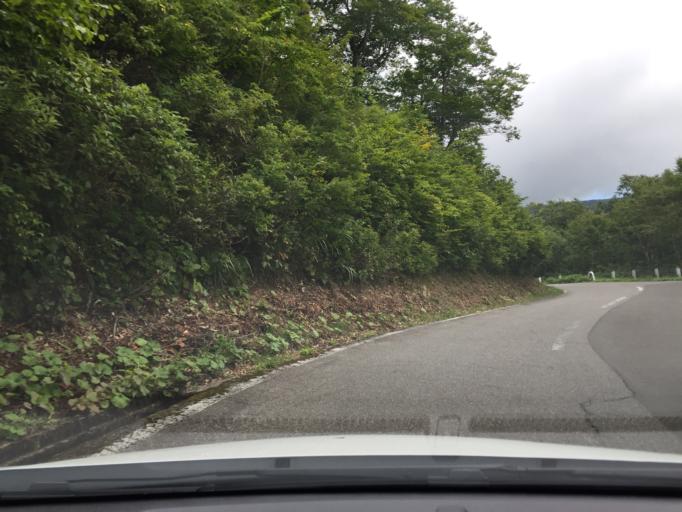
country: JP
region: Fukushima
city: Inawashiro
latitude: 37.6794
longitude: 140.2313
